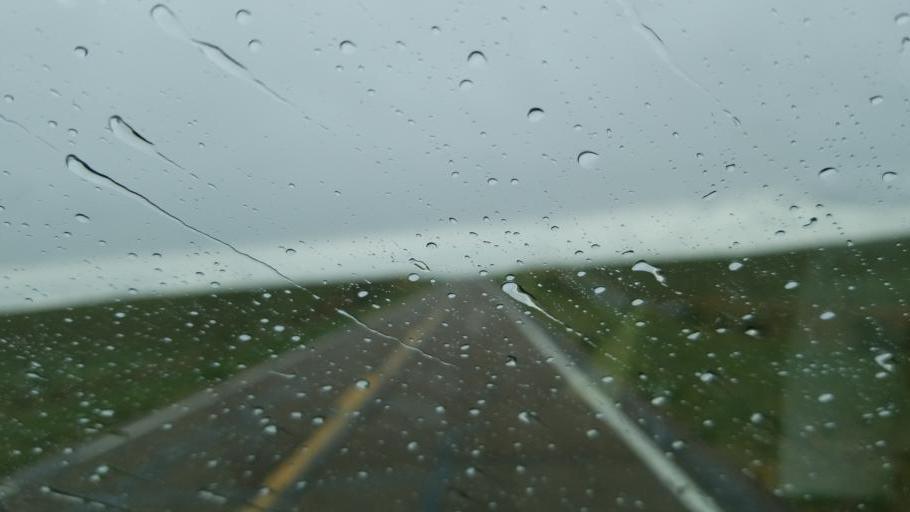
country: US
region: Colorado
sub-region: Lincoln County
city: Hugo
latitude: 38.8496
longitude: -103.2140
